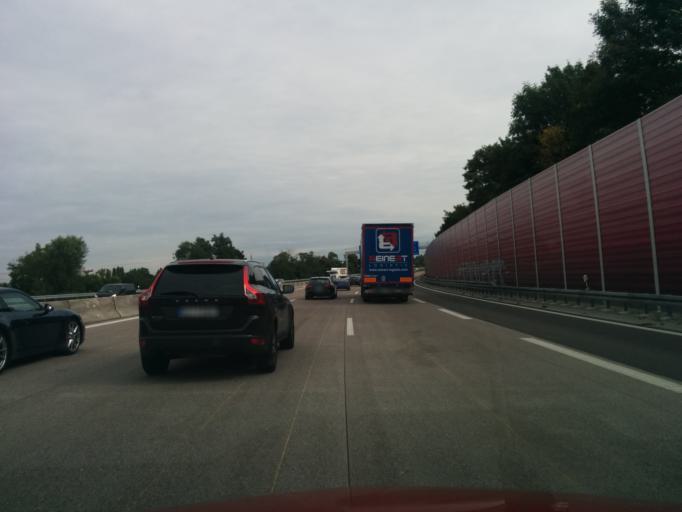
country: DE
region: Baden-Wuerttemberg
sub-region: Karlsruhe Region
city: Karlsruhe
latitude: 48.9942
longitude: 8.4379
